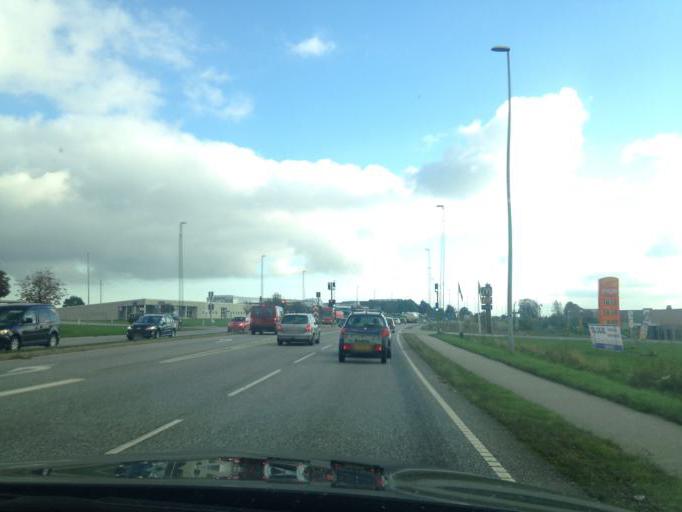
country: DK
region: South Denmark
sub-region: Vejle Kommune
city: Vejle
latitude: 55.6758
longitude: 9.5795
